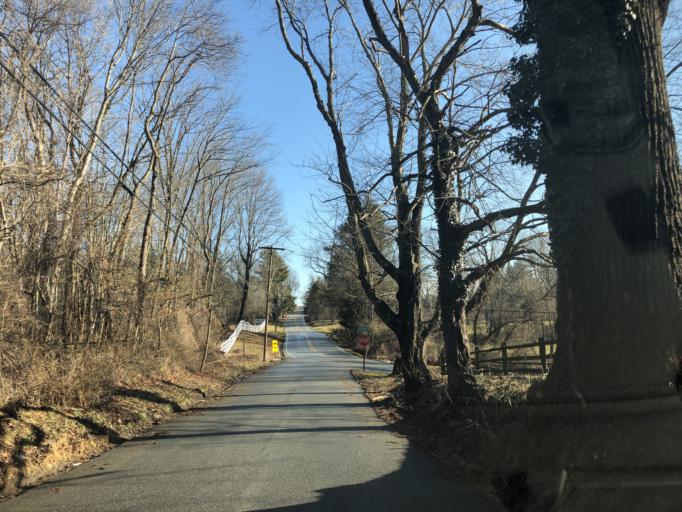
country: US
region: Pennsylvania
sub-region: Delaware County
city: Chester Heights
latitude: 39.9353
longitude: -75.4880
